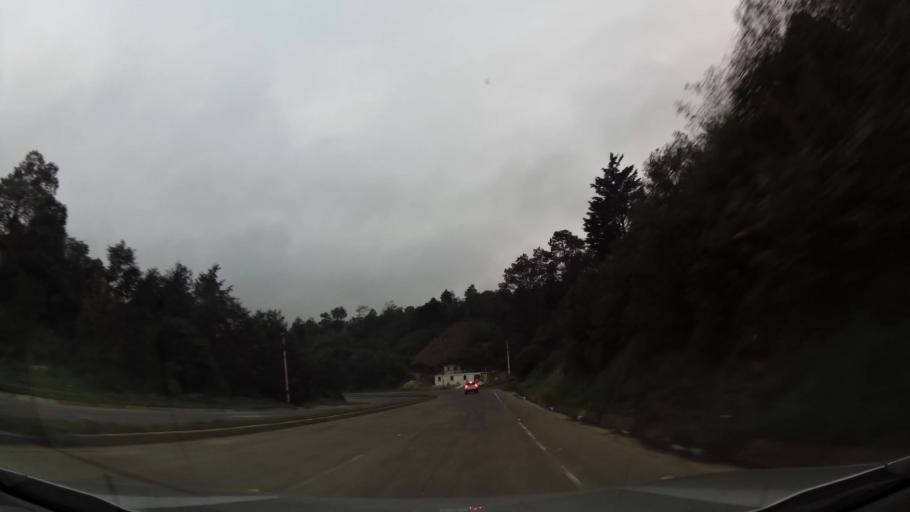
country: GT
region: Solola
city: Concepcion
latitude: 14.8248
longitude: -91.0870
